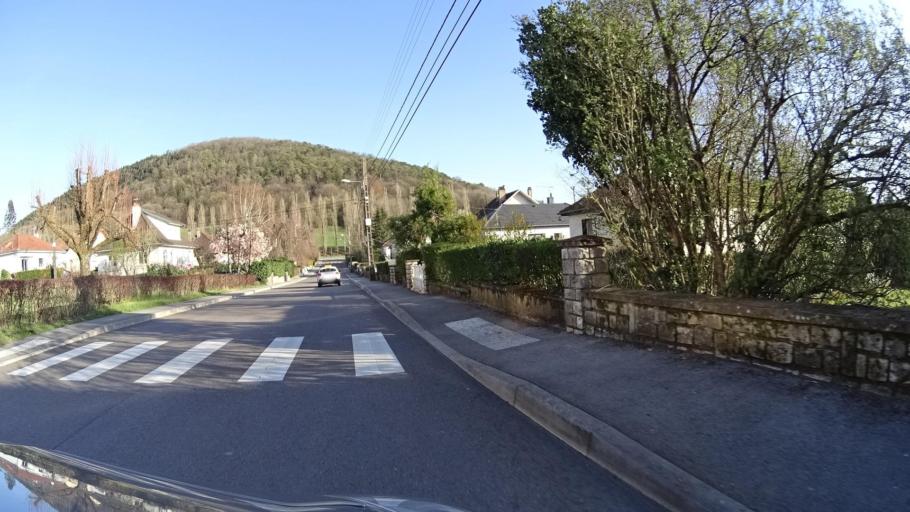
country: FR
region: Franche-Comte
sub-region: Departement du Doubs
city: Beure
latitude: 47.2258
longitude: 5.9926
